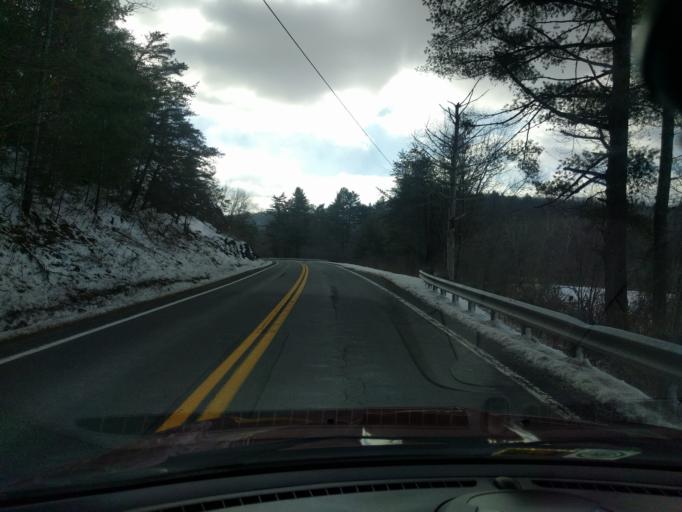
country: US
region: West Virginia
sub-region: Pocahontas County
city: Marlinton
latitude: 38.1474
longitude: -79.9823
